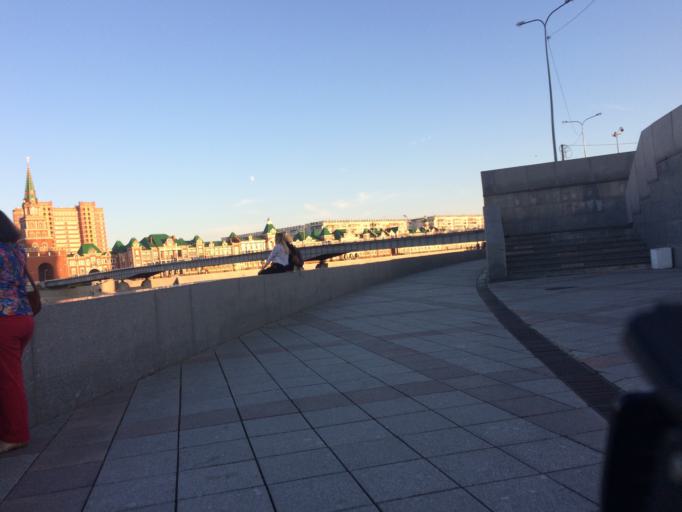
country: RU
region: Mariy-El
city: Yoshkar-Ola
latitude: 56.6342
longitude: 47.9054
